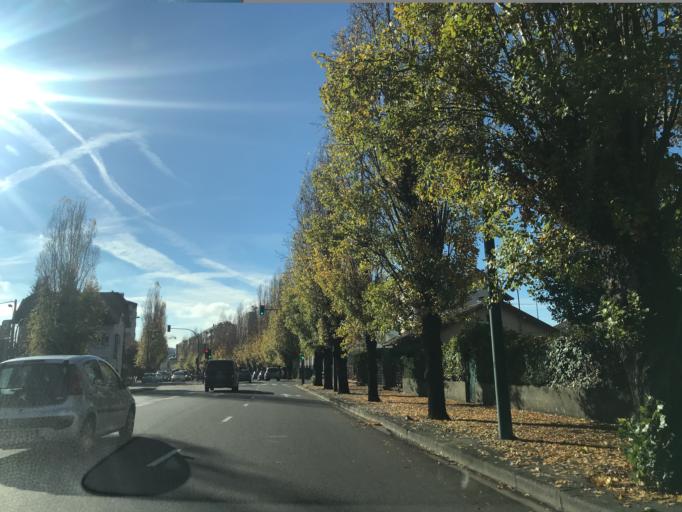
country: FR
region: Rhone-Alpes
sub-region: Departement de la Haute-Savoie
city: Annecy
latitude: 45.9099
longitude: 6.1181
